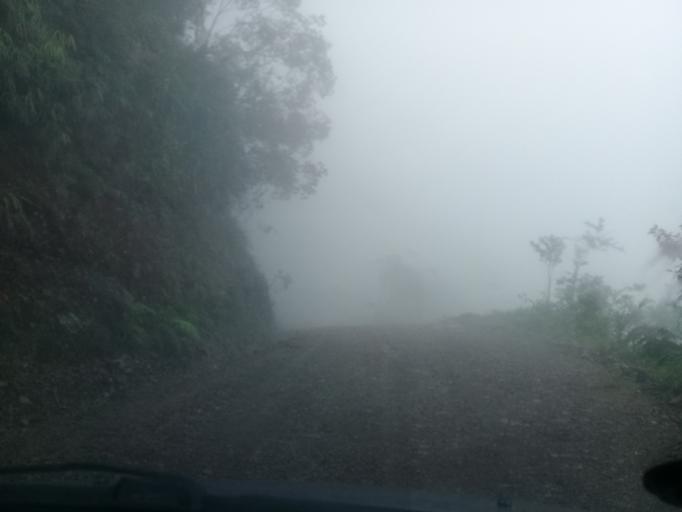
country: CO
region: Cundinamarca
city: Gachala
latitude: 4.7103
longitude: -73.4017
